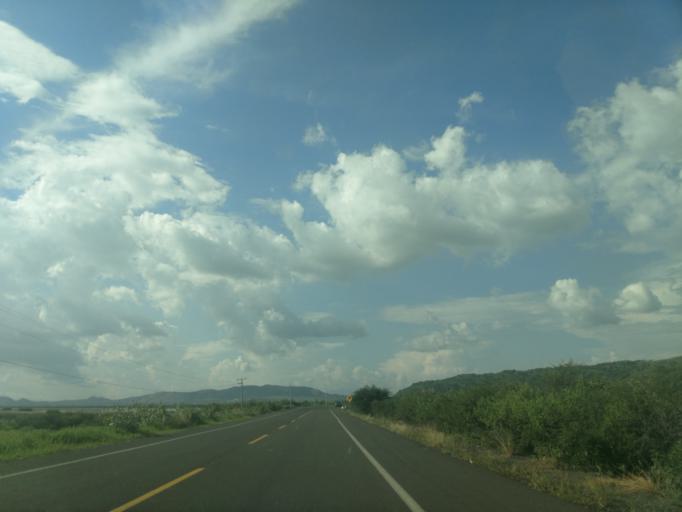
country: MX
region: Jalisco
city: Antonio Escobedo
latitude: 20.8990
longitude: -103.9948
